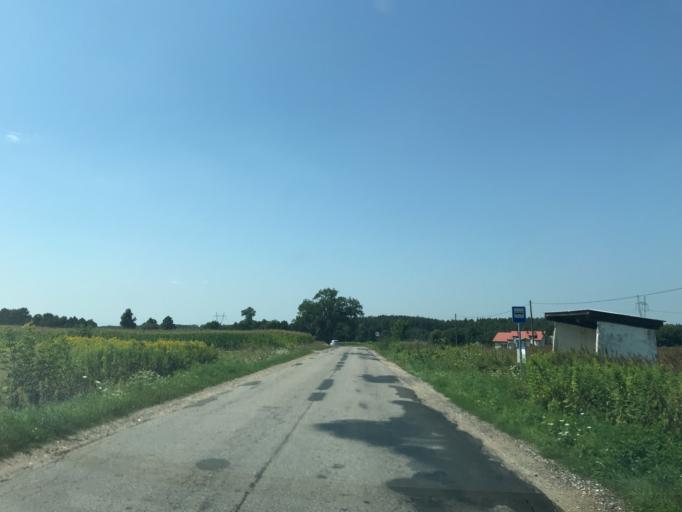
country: PL
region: Kujawsko-Pomorskie
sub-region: Powiat rypinski
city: Rogowo
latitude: 52.9847
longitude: 19.3155
